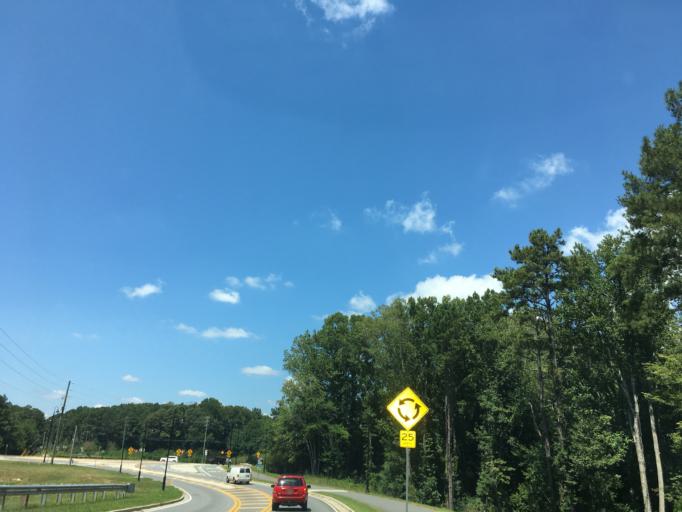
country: US
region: Georgia
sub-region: Fulton County
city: Milton
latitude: 34.1191
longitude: -84.3406
